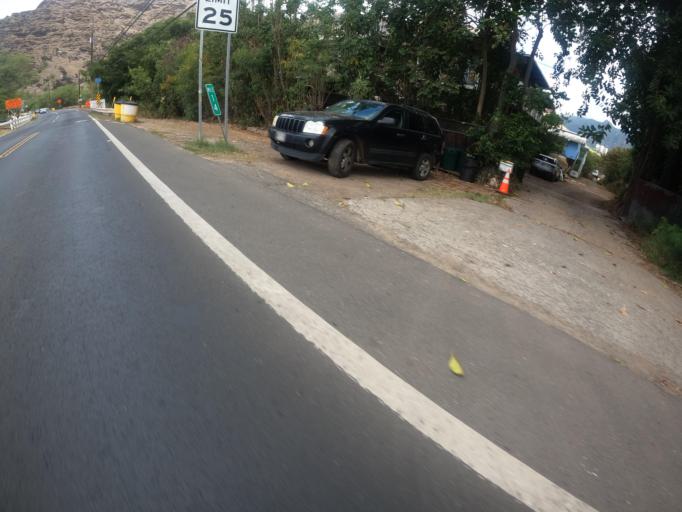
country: US
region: Hawaii
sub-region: Honolulu County
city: Makaha
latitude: 21.4757
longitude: -158.2191
